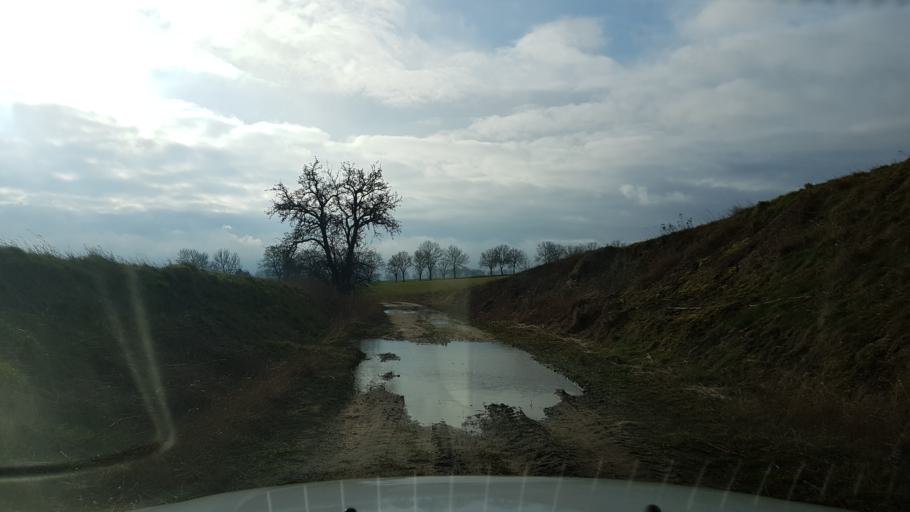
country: PL
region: West Pomeranian Voivodeship
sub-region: Powiat choszczenski
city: Pelczyce
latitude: 53.1017
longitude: 15.3327
